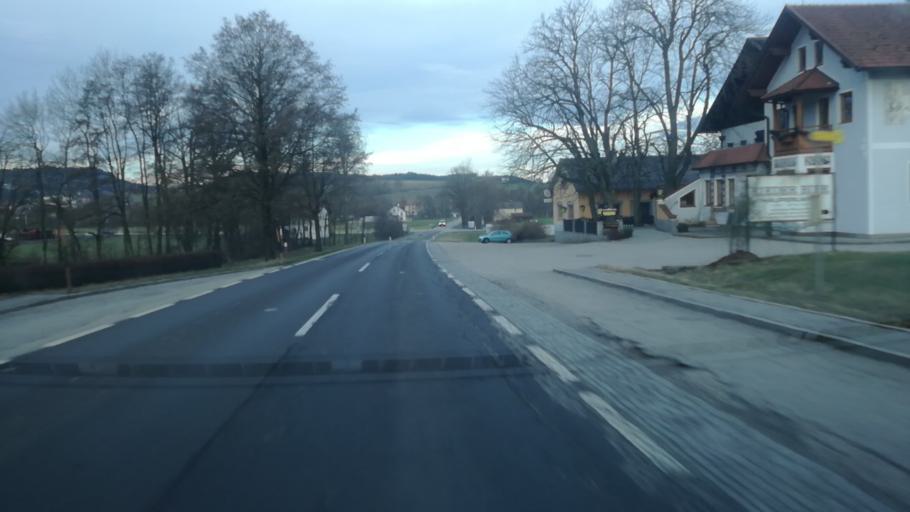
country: AT
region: Upper Austria
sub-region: Politischer Bezirk Ried im Innkreis
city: Waldzell
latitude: 48.1541
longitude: 13.4253
